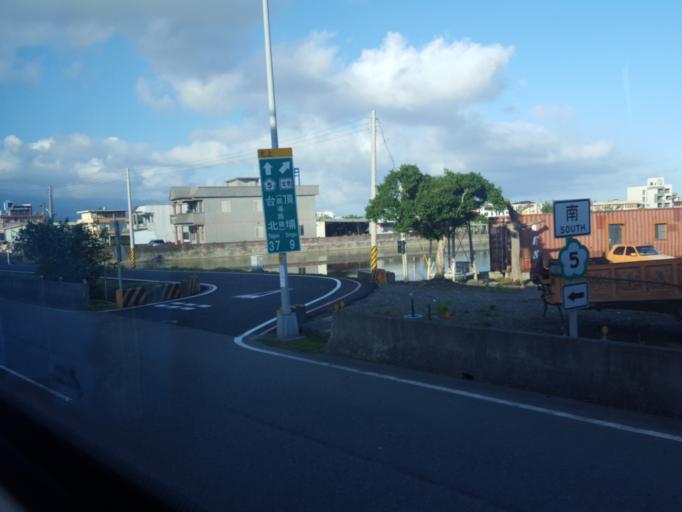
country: TW
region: Taiwan
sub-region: Yilan
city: Yilan
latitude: 24.7762
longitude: 121.7788
